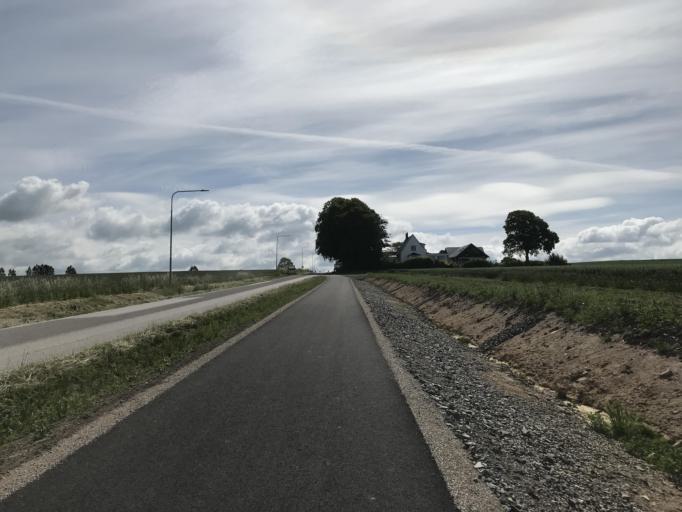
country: SE
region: Skane
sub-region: Helsingborg
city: Glumslov
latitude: 55.9416
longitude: 12.7958
